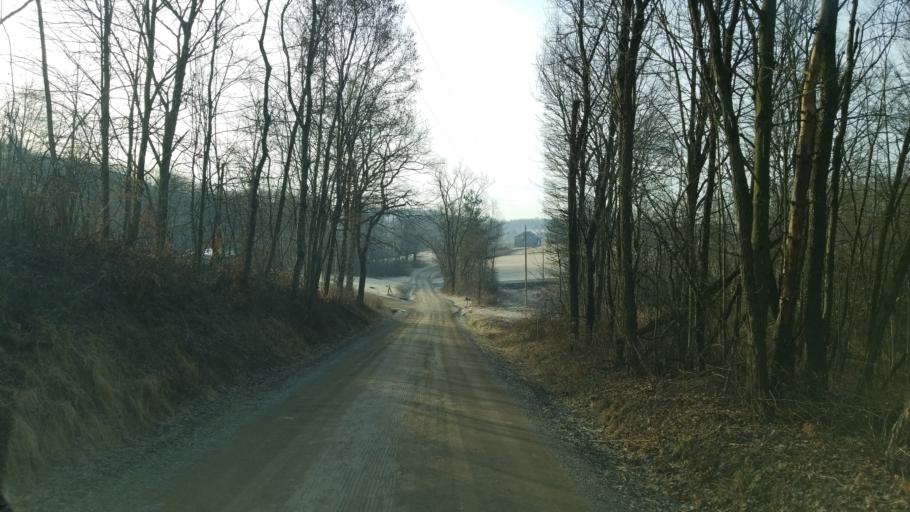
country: US
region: Pennsylvania
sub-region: Indiana County
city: Chevy Chase Heights
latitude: 40.8548
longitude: -79.2478
